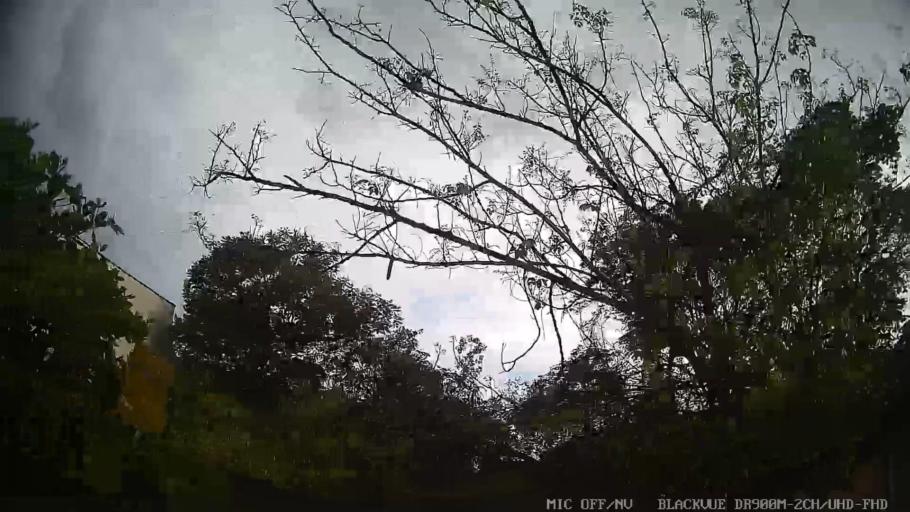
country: BR
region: Sao Paulo
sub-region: Itatiba
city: Itatiba
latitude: -23.0164
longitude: -46.8443
